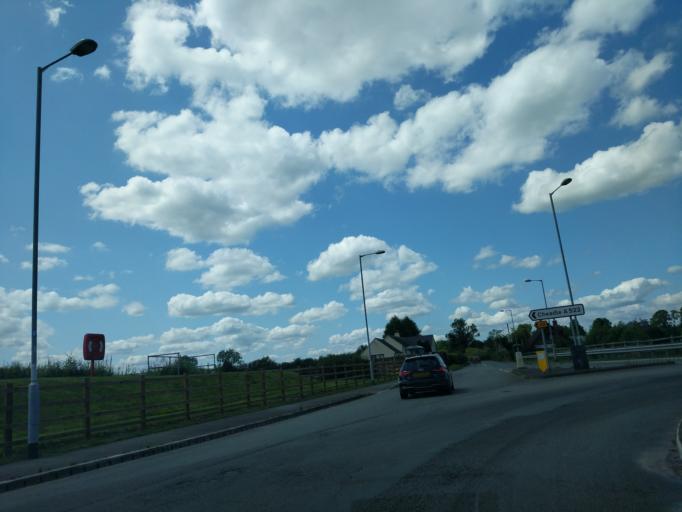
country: GB
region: England
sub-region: Staffordshire
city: Uttoxeter
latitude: 52.9191
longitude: -1.9018
